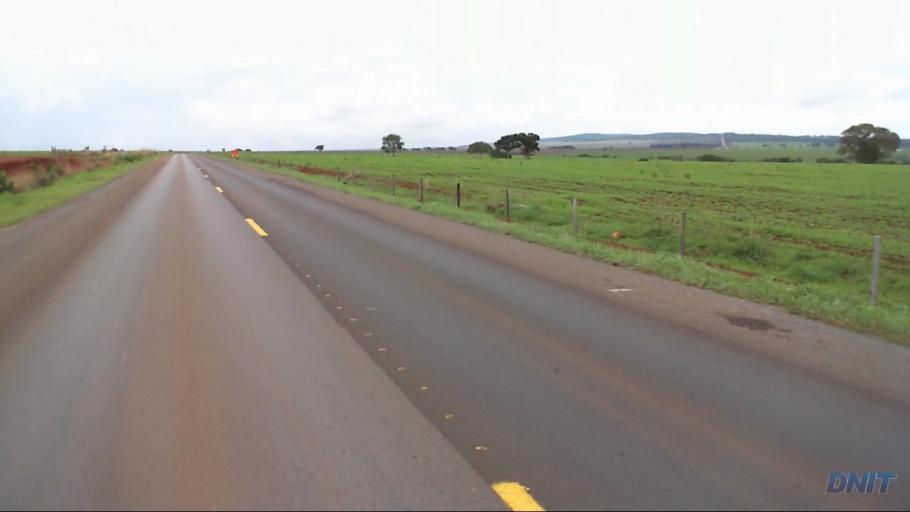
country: BR
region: Goias
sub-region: Padre Bernardo
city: Padre Bernardo
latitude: -15.1683
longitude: -48.3650
